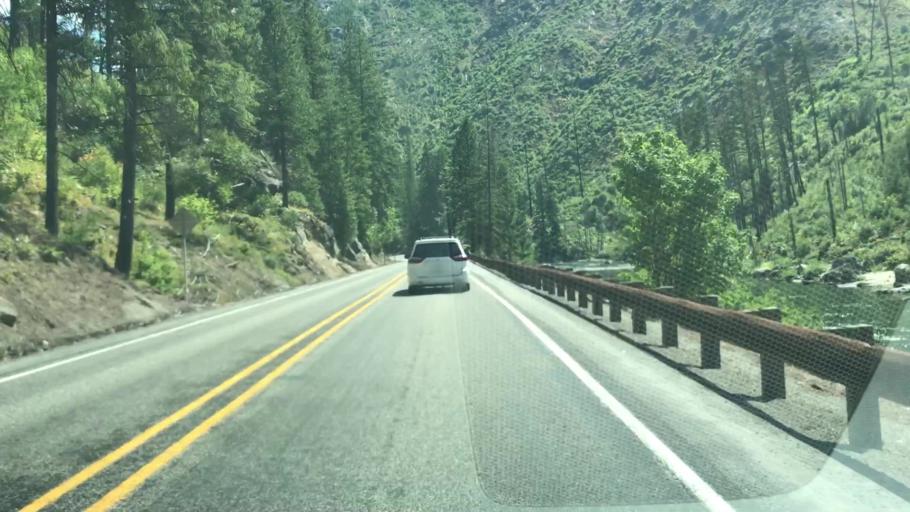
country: US
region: Washington
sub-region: Chelan County
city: Leavenworth
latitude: 47.6578
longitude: -120.7293
